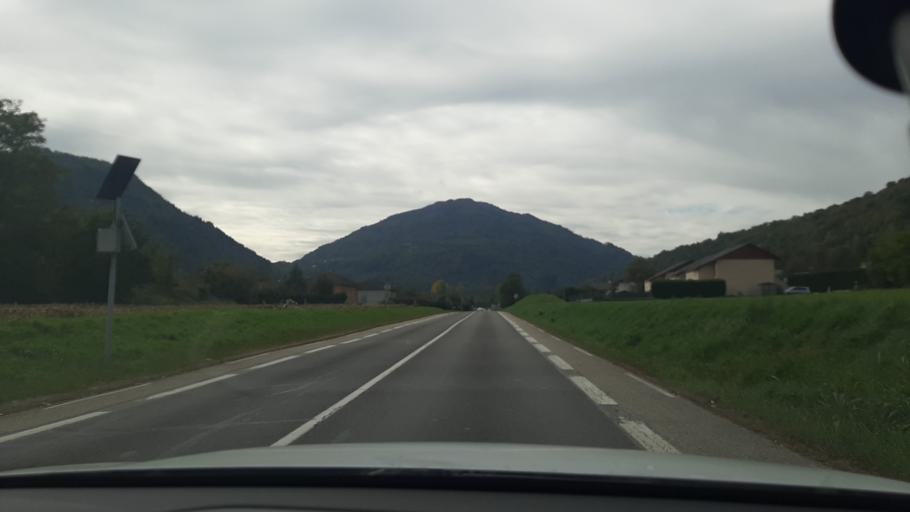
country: FR
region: Rhone-Alpes
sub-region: Departement de la Savoie
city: La Rochette
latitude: 45.4581
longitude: 6.1096
